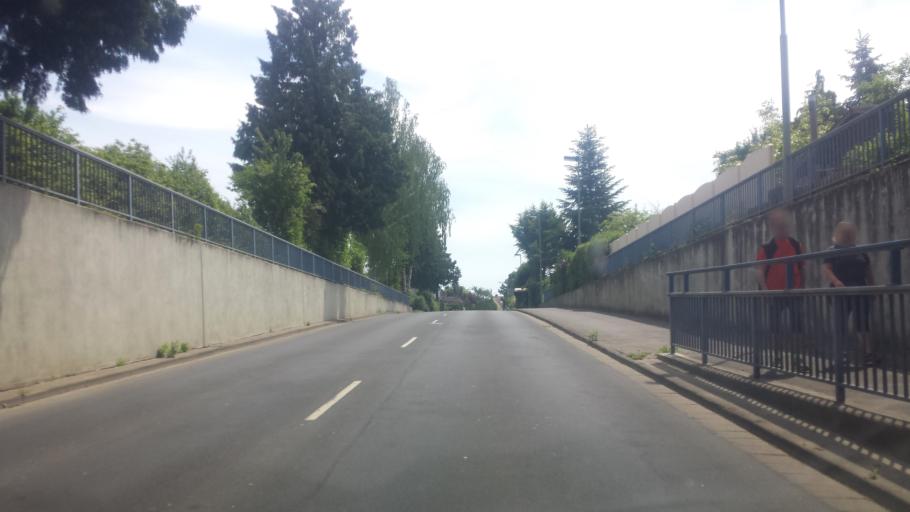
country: DE
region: Hesse
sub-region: Regierungsbezirk Darmstadt
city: Karben
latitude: 50.2100
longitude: 8.7546
